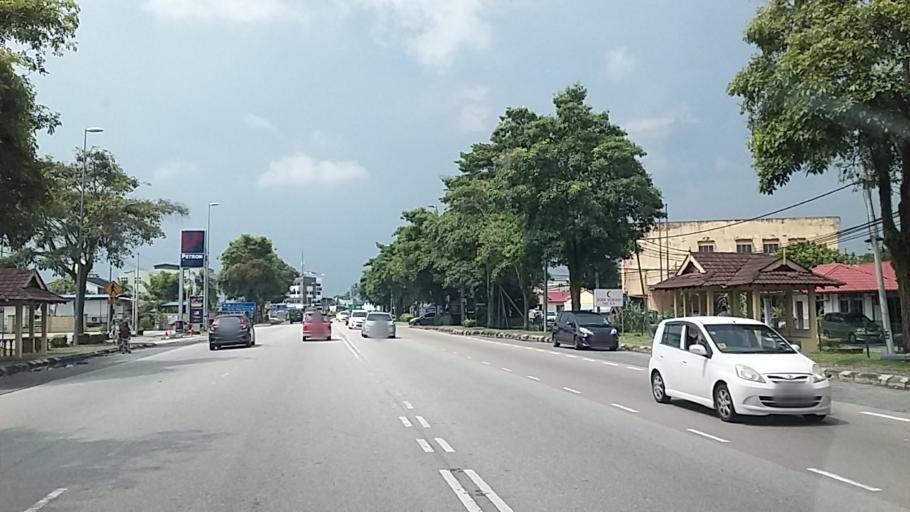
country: MY
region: Johor
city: Parit Raja
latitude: 1.8638
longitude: 103.1090
